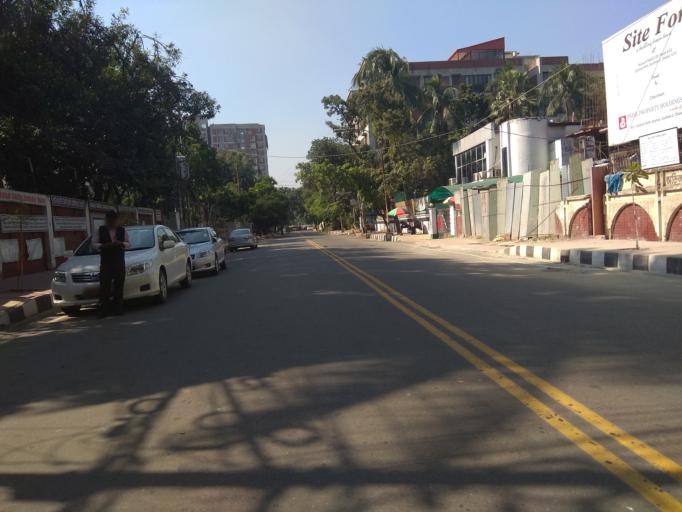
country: BD
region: Dhaka
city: Paltan
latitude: 23.8004
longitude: 90.4104
